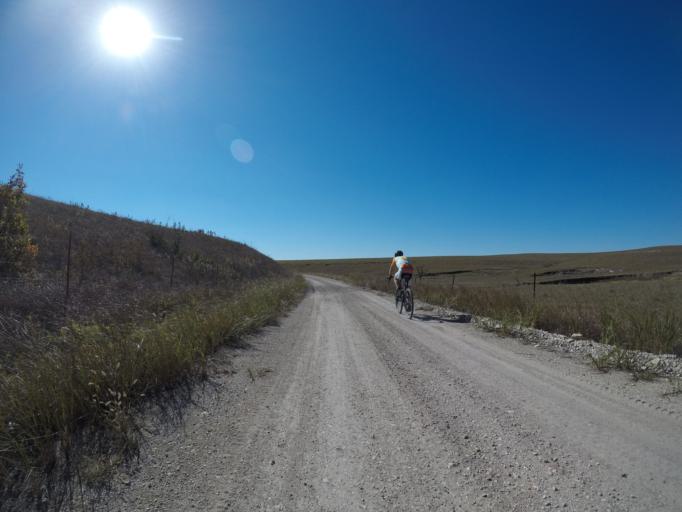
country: US
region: Kansas
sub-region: Wabaunsee County
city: Alma
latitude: 39.0222
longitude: -96.4099
